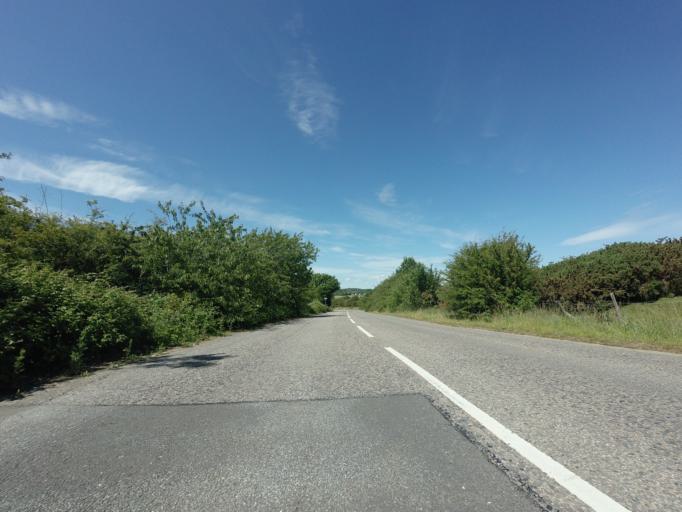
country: GB
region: England
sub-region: Kent
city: Strood
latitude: 51.4183
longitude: 0.5179
